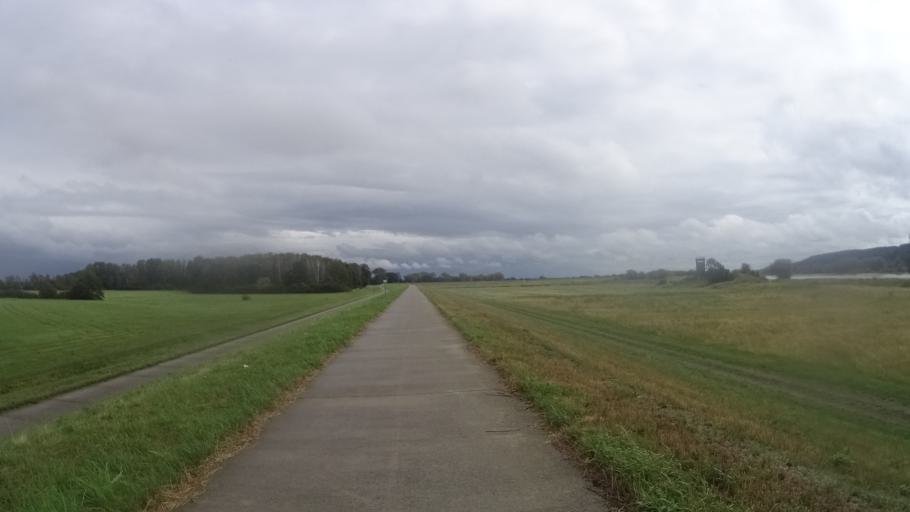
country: DE
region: Lower Saxony
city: Neu Darchau
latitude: 53.2360
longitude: 10.8989
